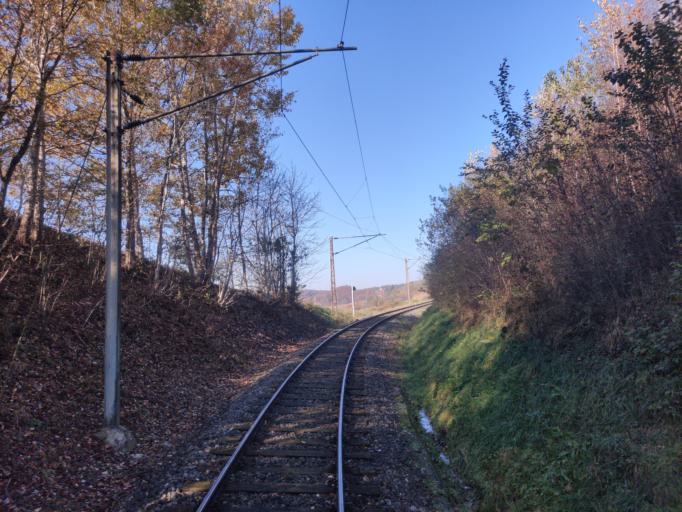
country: AT
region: Styria
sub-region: Politischer Bezirk Suedoststeiermark
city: Trautmannsdorf in Oststeiermark
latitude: 46.8794
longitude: 15.8847
